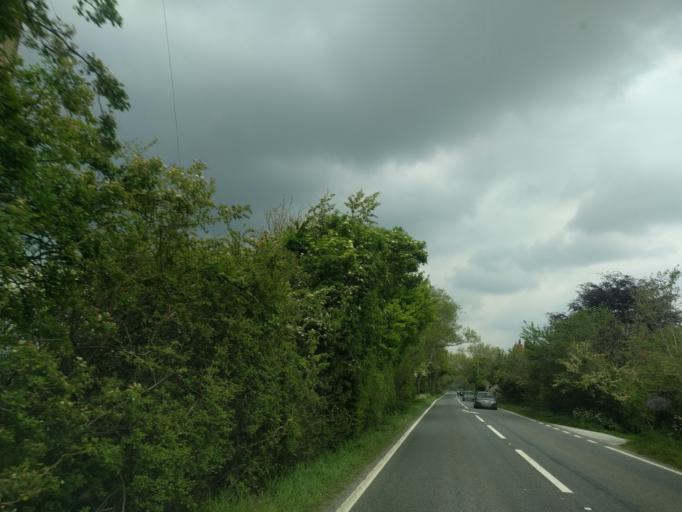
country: GB
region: England
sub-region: Somerset
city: Castle Cary
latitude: 51.1128
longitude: -2.5840
